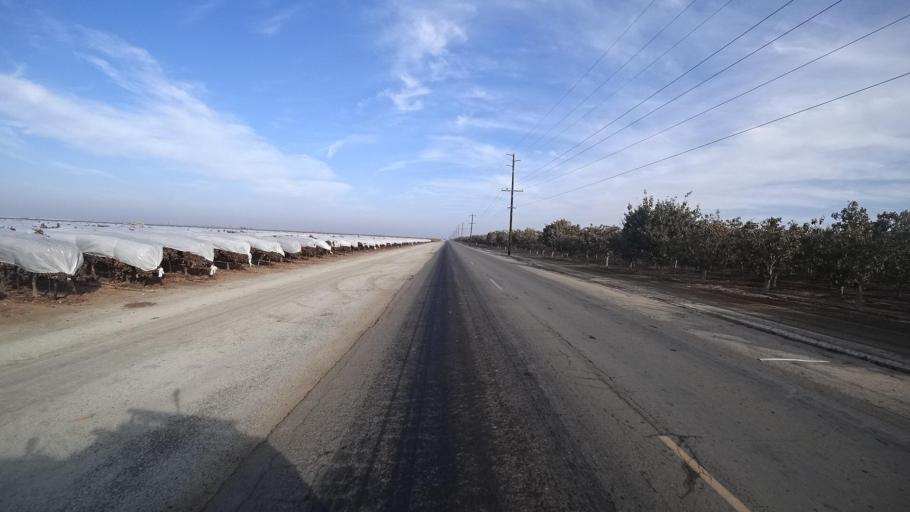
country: US
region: California
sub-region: Kern County
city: McFarland
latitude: 35.7192
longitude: -119.2051
